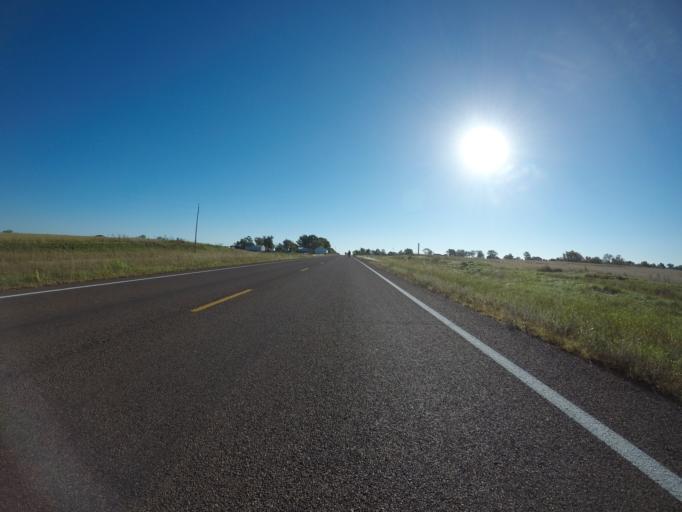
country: US
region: Kansas
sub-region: Douglas County
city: Eudora
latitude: 39.0038
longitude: -95.0982
